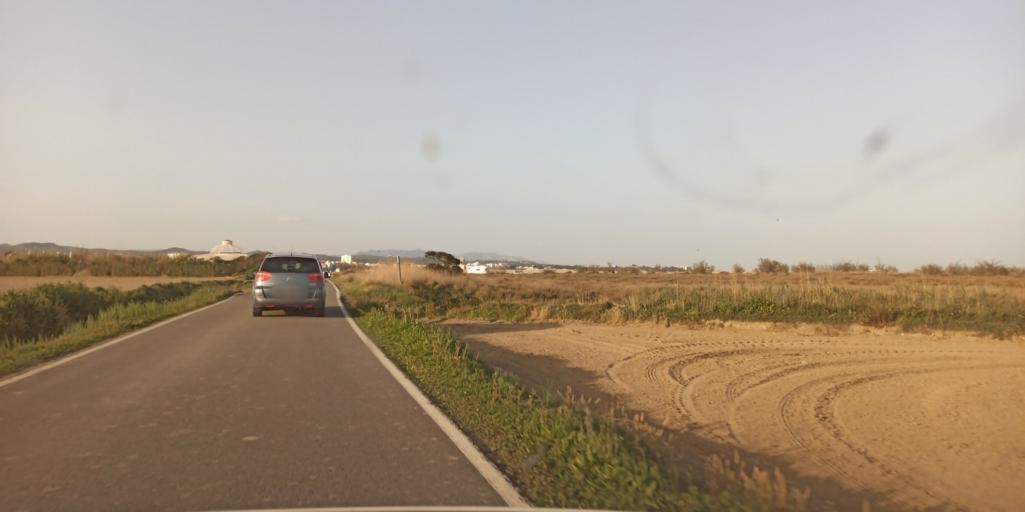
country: ES
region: Catalonia
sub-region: Provincia de Tarragona
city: L'Ampolla
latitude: 40.7951
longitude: 0.6995
